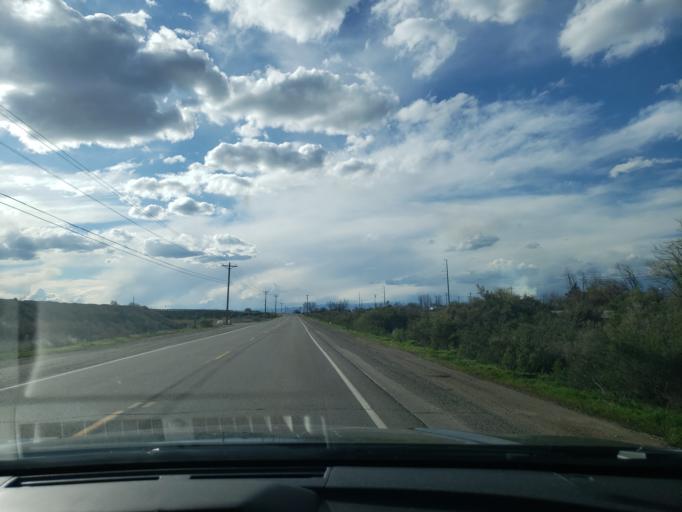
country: US
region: Colorado
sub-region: Mesa County
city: Fruita
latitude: 39.1272
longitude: -108.6796
